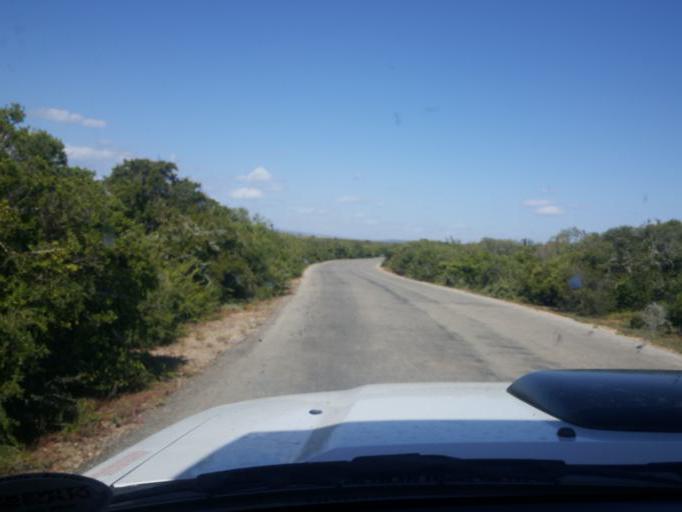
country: ZA
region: Eastern Cape
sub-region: Cacadu District Municipality
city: Kirkwood
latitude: -33.4412
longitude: 25.7606
